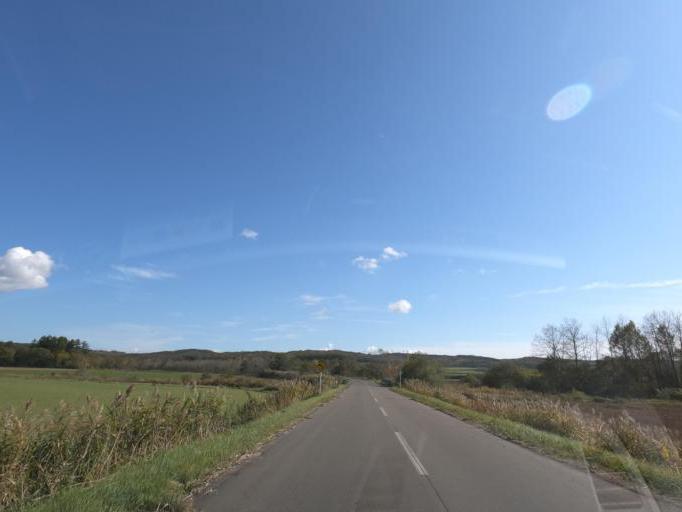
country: JP
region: Hokkaido
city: Otofuke
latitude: 43.0596
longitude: 143.2752
